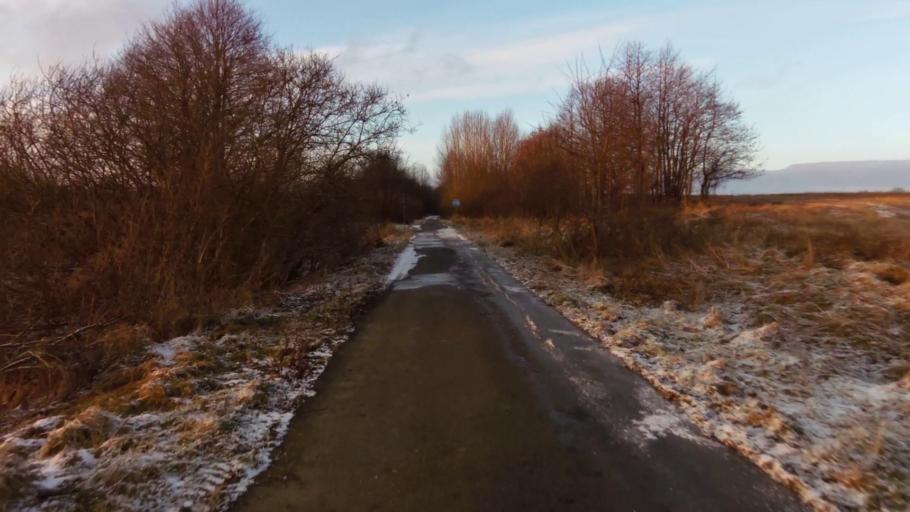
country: PL
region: West Pomeranian Voivodeship
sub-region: Powiat swidwinski
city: Polczyn-Zdroj
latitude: 53.6814
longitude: 16.0314
